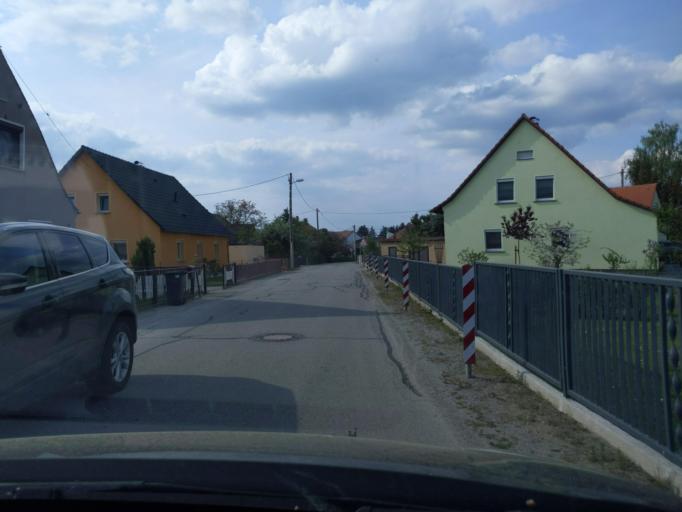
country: DE
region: Saxony
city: Malschwitz
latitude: 51.2361
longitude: 14.5243
